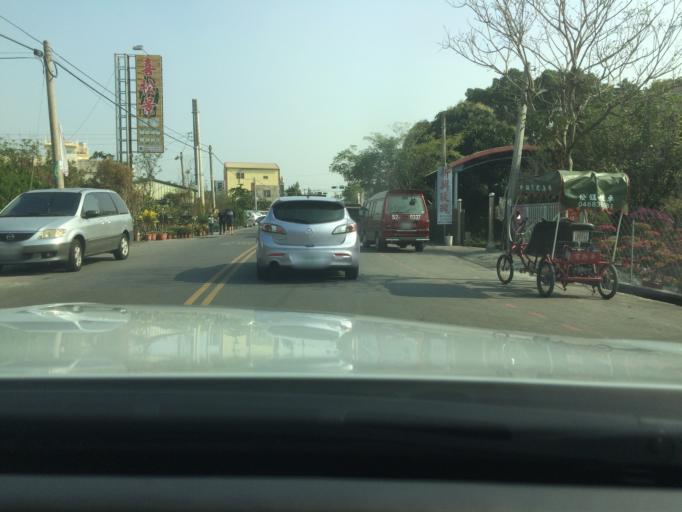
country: TW
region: Taiwan
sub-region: Nantou
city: Nantou
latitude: 23.9003
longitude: 120.5294
